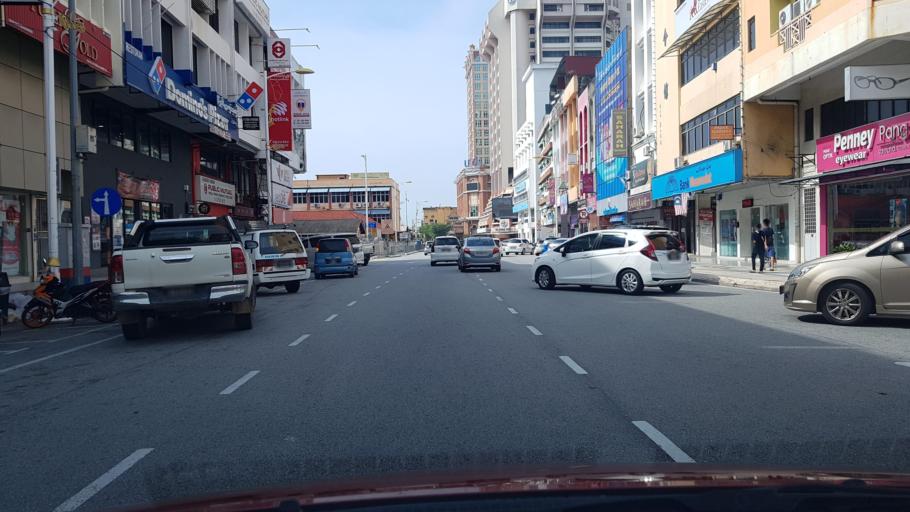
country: MY
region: Terengganu
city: Kuala Terengganu
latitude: 5.3287
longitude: 103.1354
